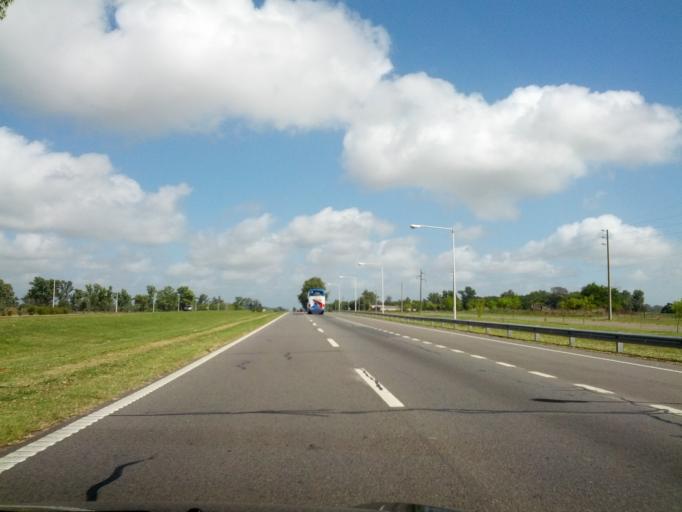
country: AR
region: Buenos Aires
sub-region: Partido de Mercedes
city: Mercedes
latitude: -34.6491
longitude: -59.3166
